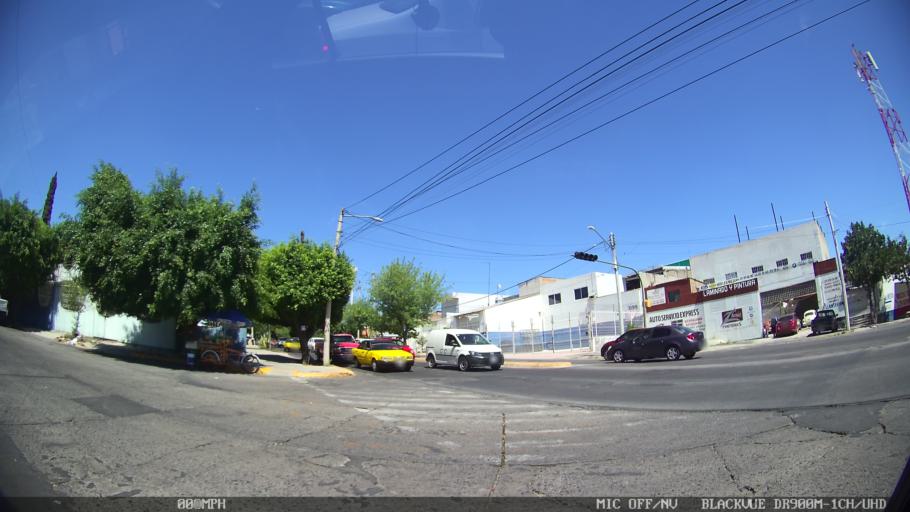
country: MX
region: Jalisco
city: Tlaquepaque
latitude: 20.7015
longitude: -103.2853
